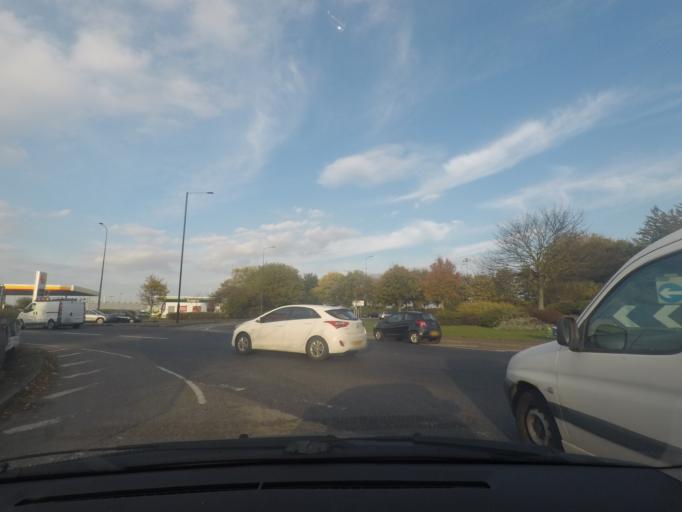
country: GB
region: England
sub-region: North East Lincolnshire
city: Grimbsy
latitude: 53.5750
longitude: -0.0972
